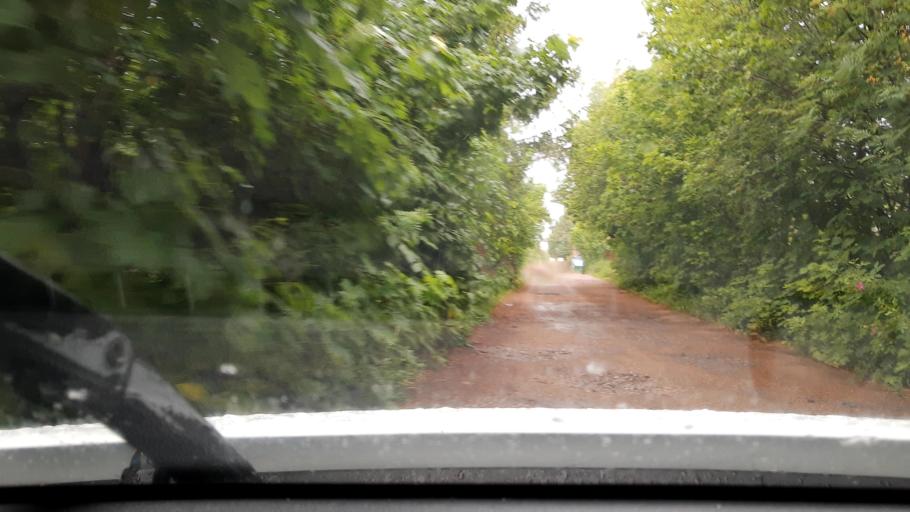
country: RU
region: Bashkortostan
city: Karmaskaly
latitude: 54.3802
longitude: 55.9099
